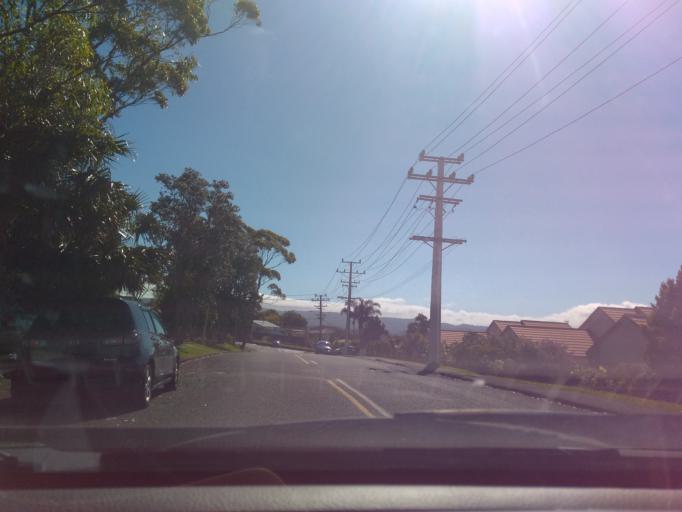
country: NZ
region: Auckland
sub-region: Auckland
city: Waitakere
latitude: -36.8976
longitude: 174.6447
